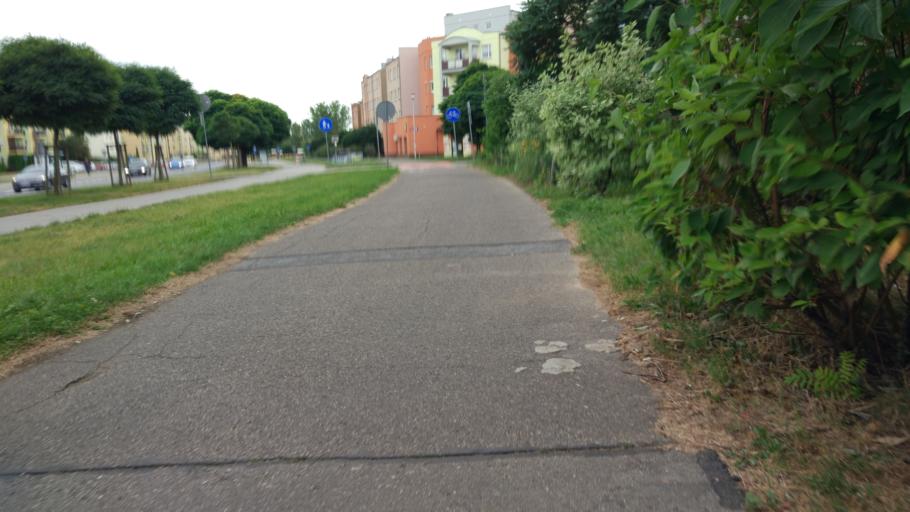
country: PL
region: Masovian Voivodeship
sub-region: Plock
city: Plock
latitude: 52.5329
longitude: 19.7582
